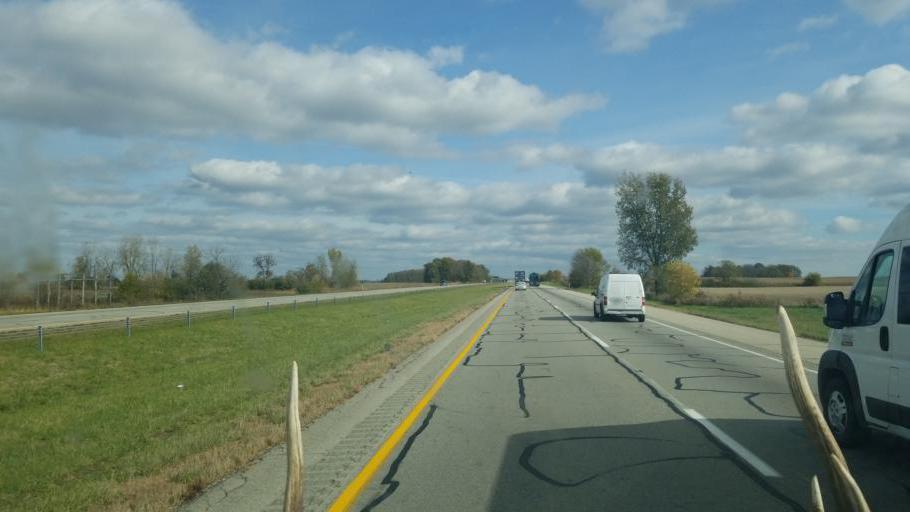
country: US
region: Indiana
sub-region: Henry County
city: New Castle
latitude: 39.8532
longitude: -85.3232
